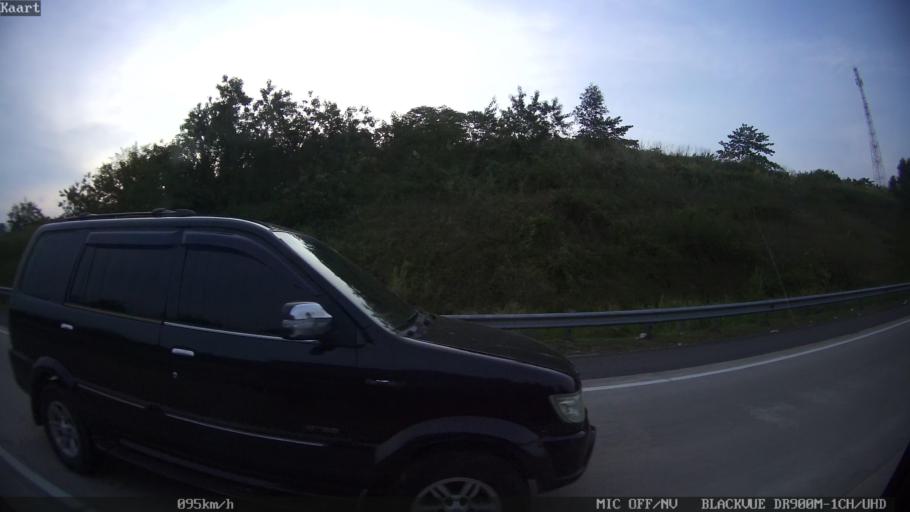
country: ID
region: Lampung
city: Penengahan
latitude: -5.8215
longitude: 105.7353
